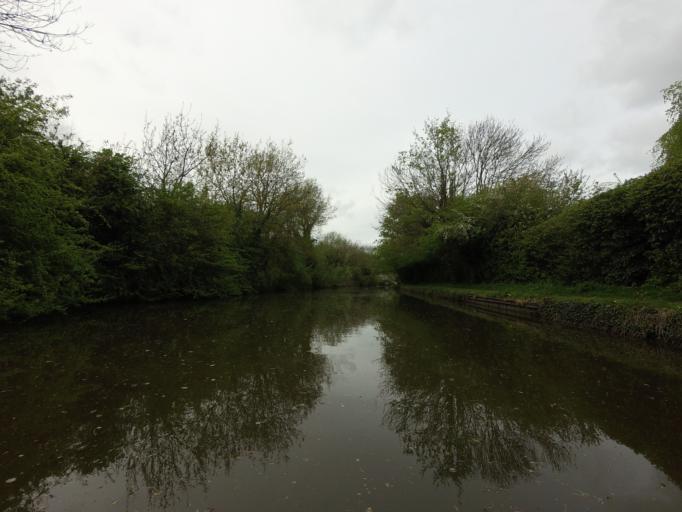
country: GB
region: England
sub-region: Milton Keynes
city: Simpson
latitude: 52.0219
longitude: -0.7214
